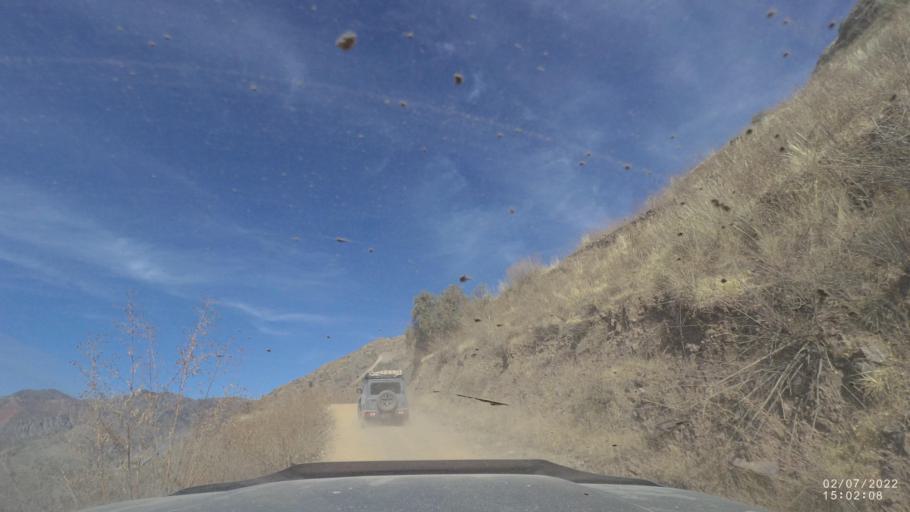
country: BO
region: Cochabamba
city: Irpa Irpa
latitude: -17.8556
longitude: -66.4403
